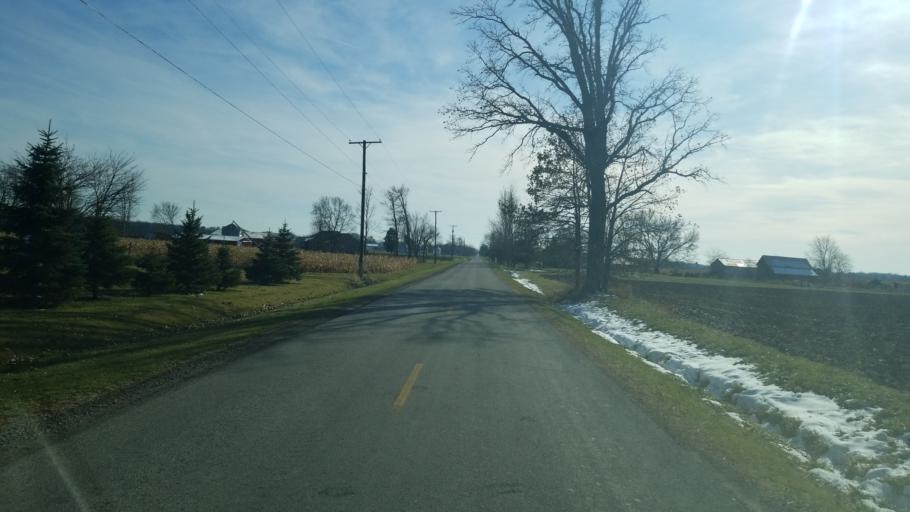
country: US
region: Ohio
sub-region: Huron County
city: New London
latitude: 41.1336
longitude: -82.3490
